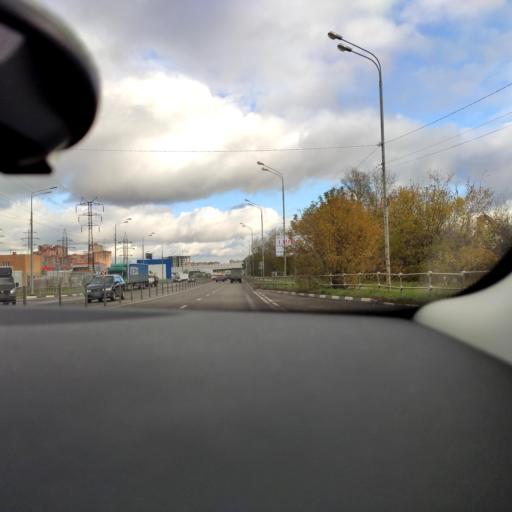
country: RU
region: Moskovskaya
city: Kotel'niki
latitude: 55.6503
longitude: 37.8485
